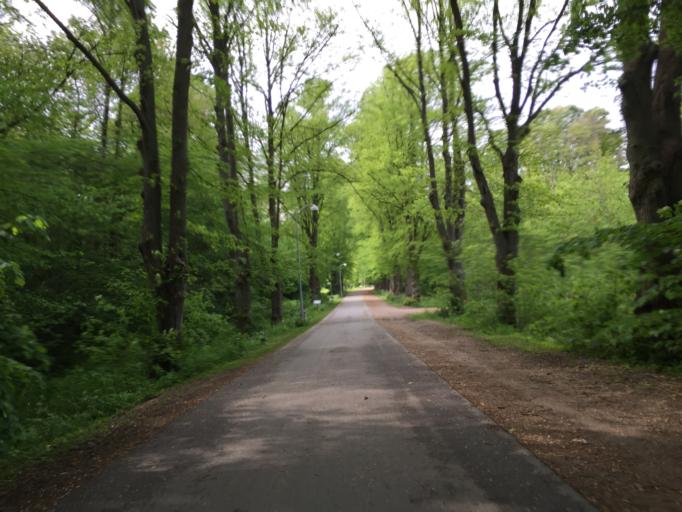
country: DK
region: Capital Region
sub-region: Brondby Kommune
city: Brondbyvester
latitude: 55.6239
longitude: 12.4448
